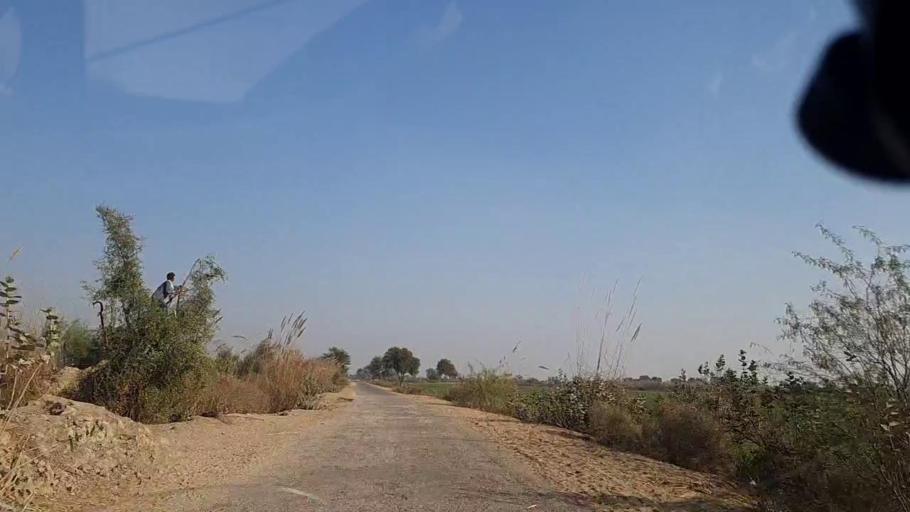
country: PK
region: Sindh
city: Khanpur
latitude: 27.6865
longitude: 69.5198
